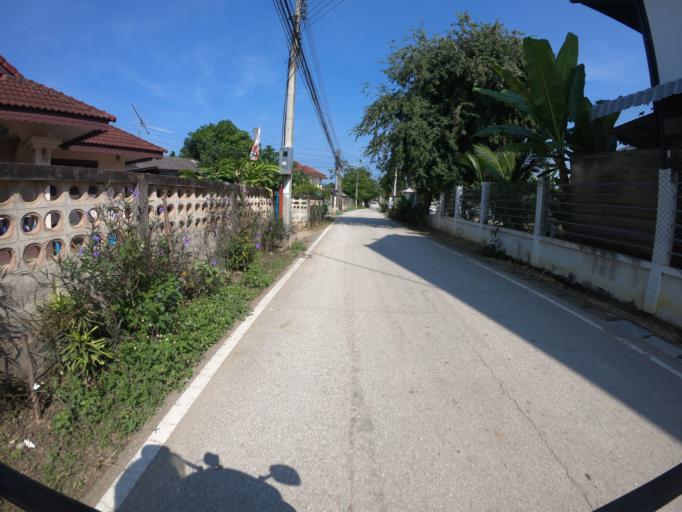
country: TH
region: Chiang Mai
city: San Sai
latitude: 18.8646
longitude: 98.9805
